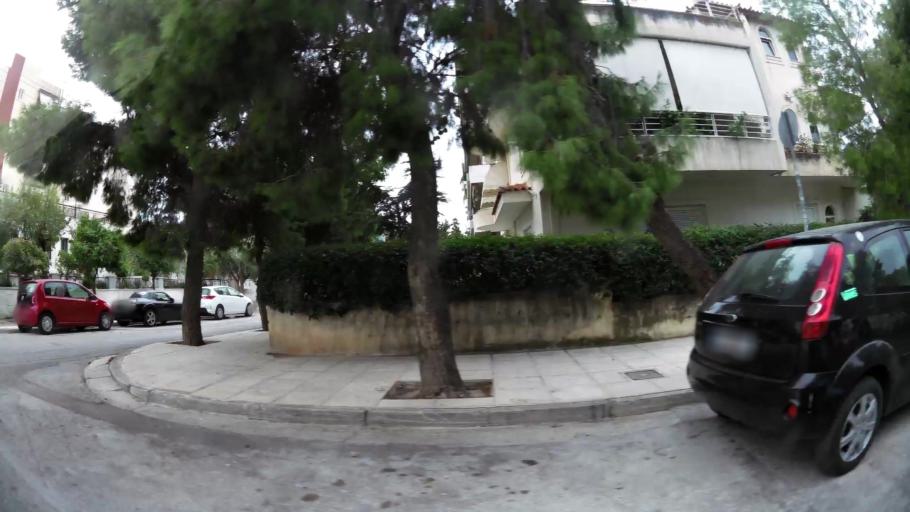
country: GR
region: Attica
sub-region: Nomarchia Athinas
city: Alimos
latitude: 37.9250
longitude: 23.7196
